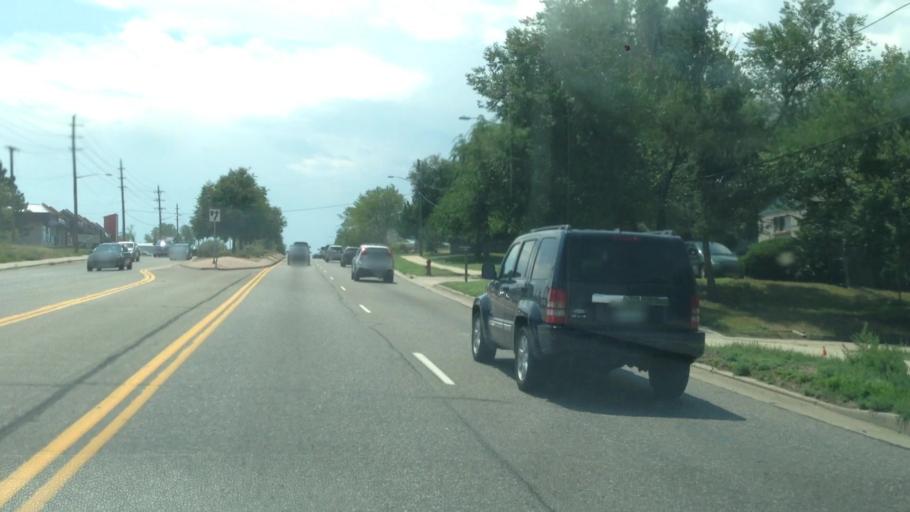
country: US
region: Colorado
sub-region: Jefferson County
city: Lakewood
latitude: 39.6997
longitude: -105.0816
